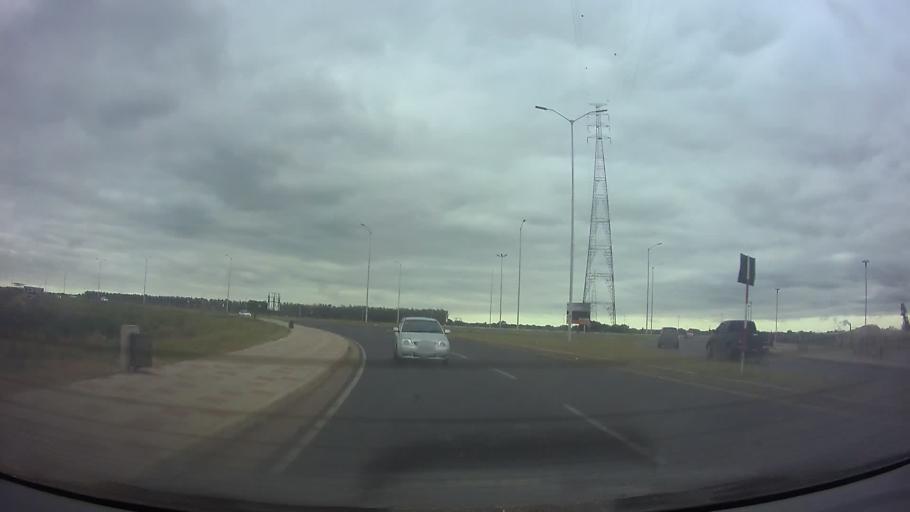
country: PY
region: Asuncion
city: Asuncion
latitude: -25.2453
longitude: -57.5901
